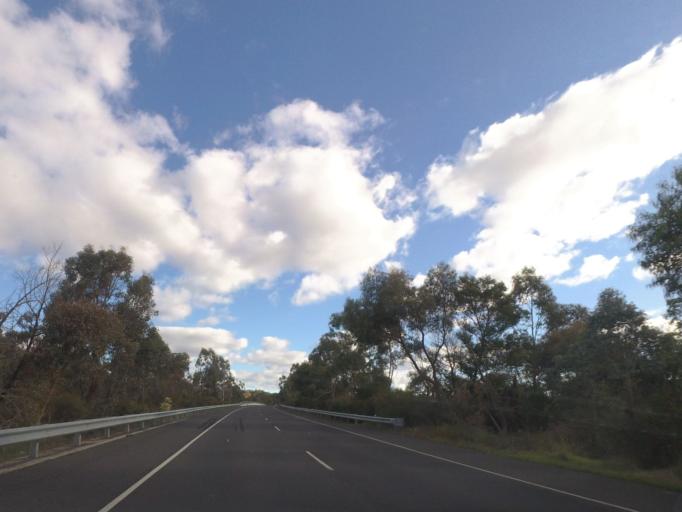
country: AU
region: Victoria
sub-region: Mount Alexander
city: Castlemaine
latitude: -37.1010
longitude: 144.3212
